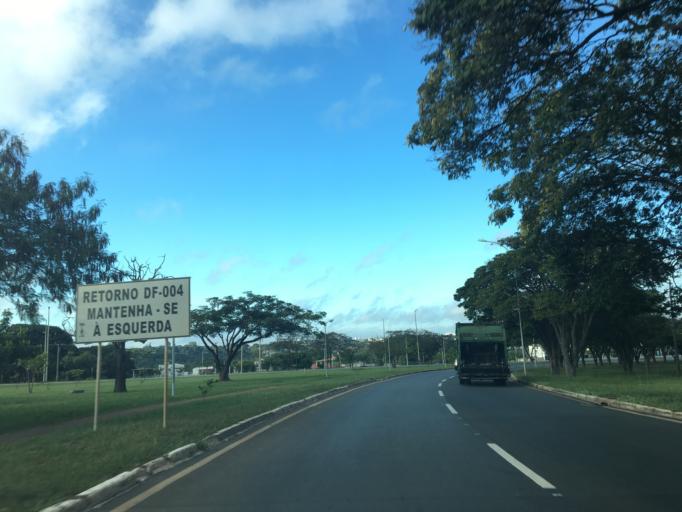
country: BR
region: Federal District
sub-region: Brasilia
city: Brasilia
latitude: -15.8433
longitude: -47.9204
